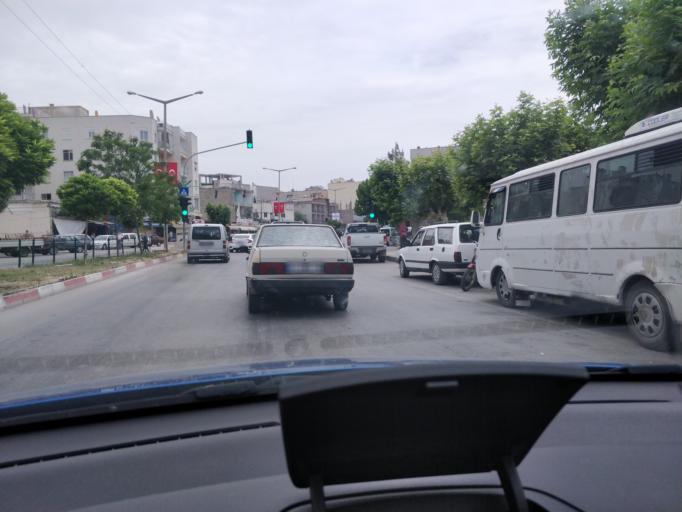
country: TR
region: Mersin
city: Mut
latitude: 36.6463
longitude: 33.4348
